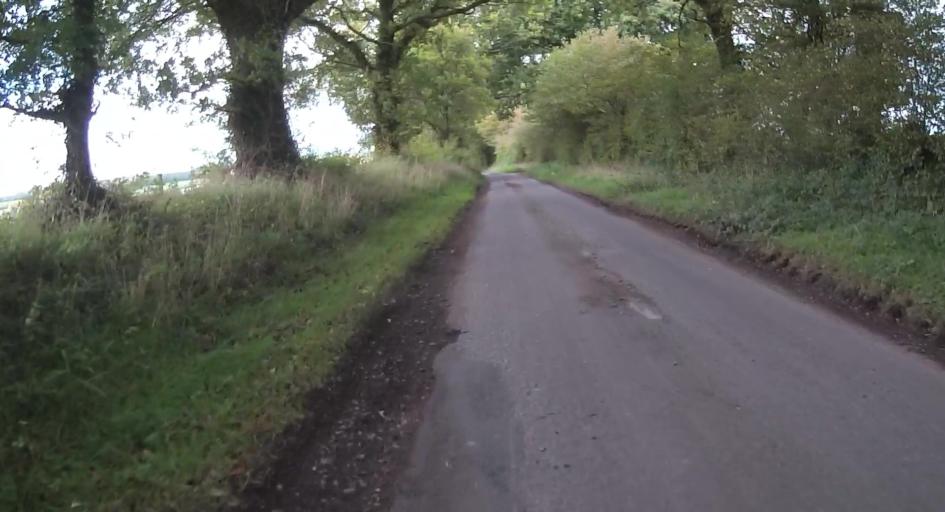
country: GB
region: England
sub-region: Hampshire
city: Alton
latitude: 51.1614
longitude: -0.9261
